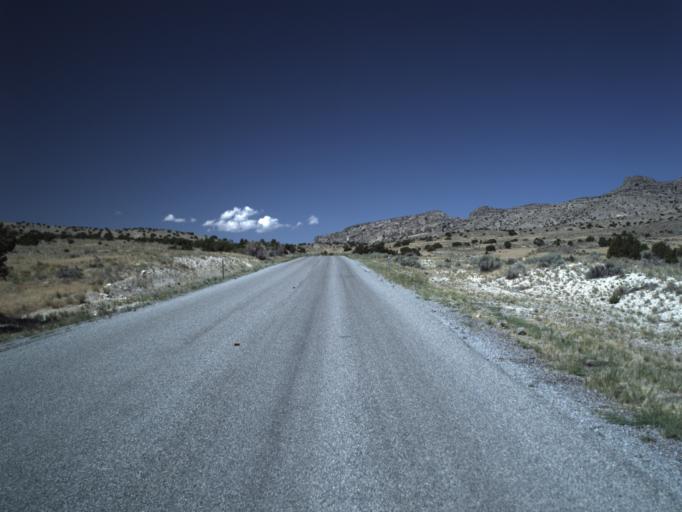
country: US
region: Utah
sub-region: Beaver County
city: Milford
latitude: 39.0770
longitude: -113.6244
